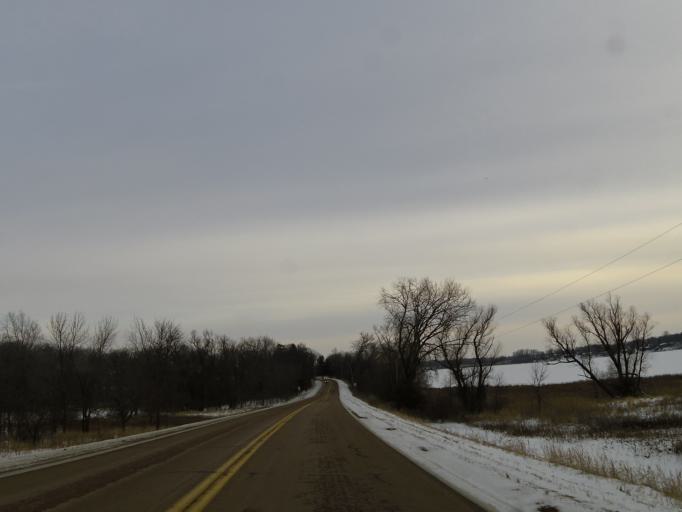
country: US
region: Minnesota
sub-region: Carver County
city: Victoria
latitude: 44.8711
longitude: -93.6801
